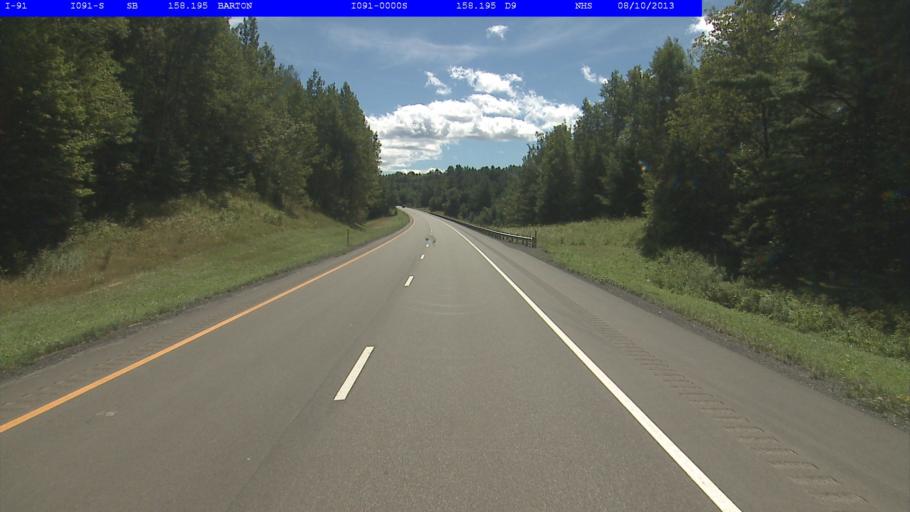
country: US
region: Vermont
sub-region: Orleans County
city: Newport
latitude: 44.7614
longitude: -72.2081
